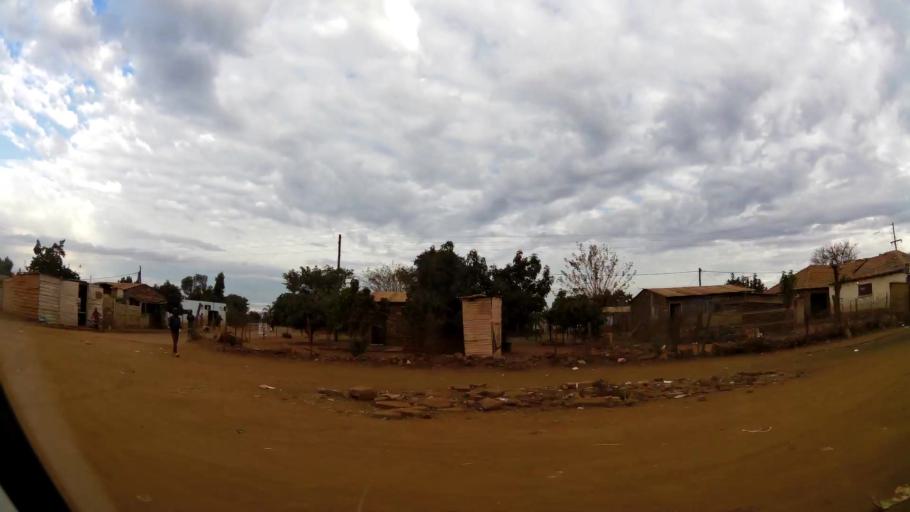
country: ZA
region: Limpopo
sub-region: Waterberg District Municipality
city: Modimolle
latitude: -24.5266
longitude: 28.7192
